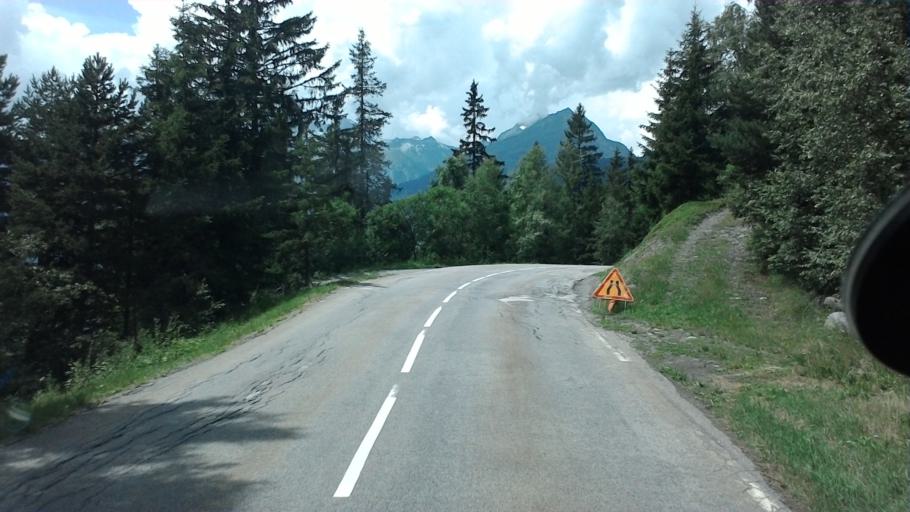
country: FR
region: Rhone-Alpes
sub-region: Departement de la Savoie
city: Seez
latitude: 45.6228
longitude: 6.8386
